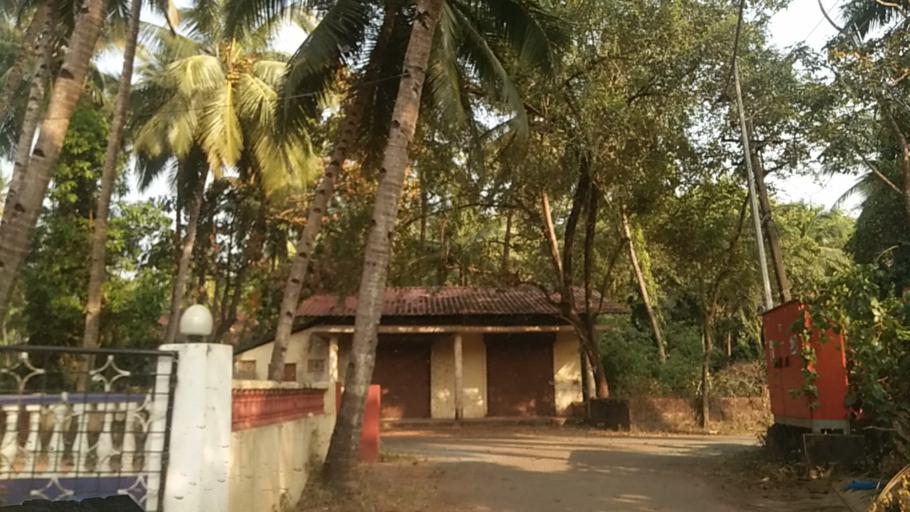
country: IN
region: Goa
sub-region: South Goa
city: Colva
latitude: 15.3126
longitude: 73.9336
